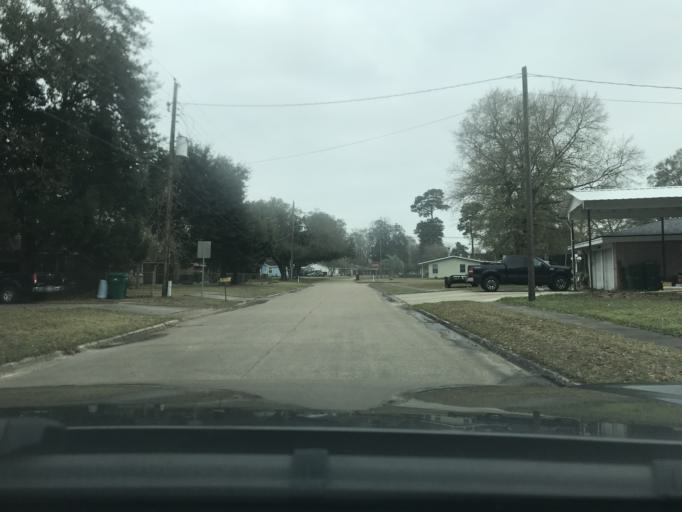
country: US
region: Louisiana
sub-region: Calcasieu Parish
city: Westlake
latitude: 30.2523
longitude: -93.2553
